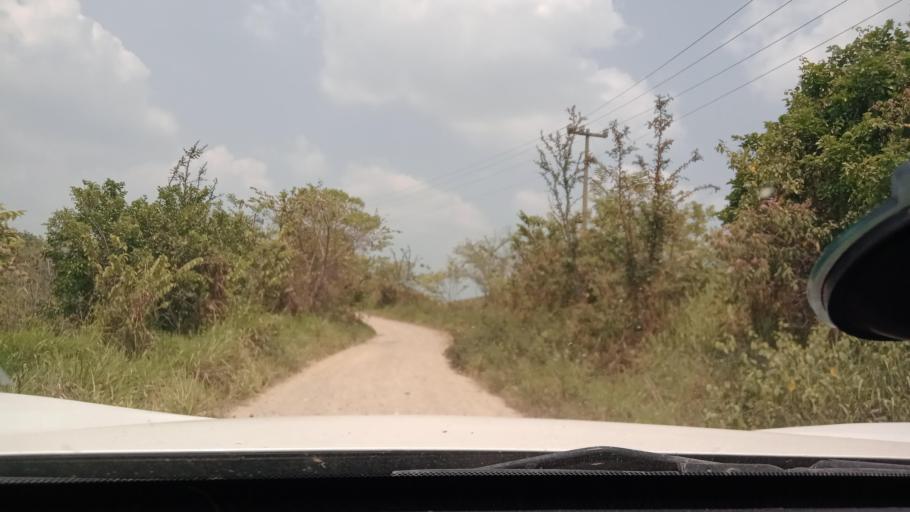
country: MX
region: Tabasco
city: Chontalpa
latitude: 17.5783
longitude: -93.7019
